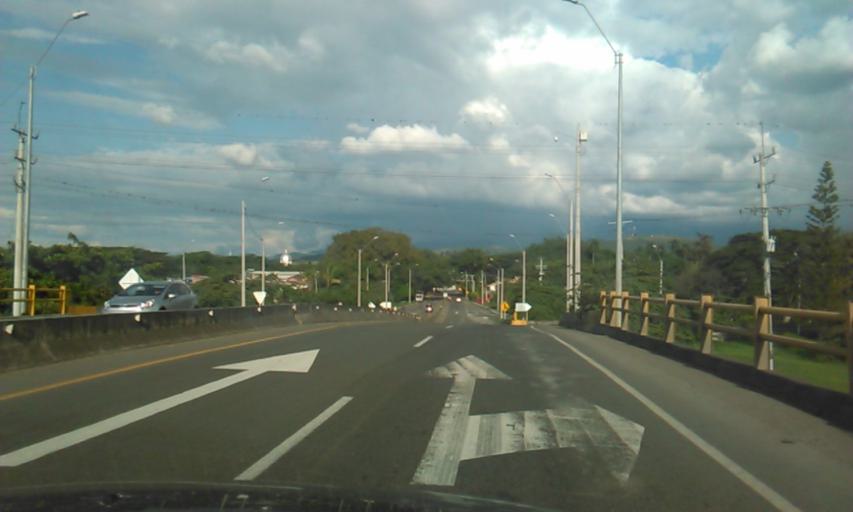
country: CO
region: Valle del Cauca
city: Buga
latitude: 3.8933
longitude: -76.3122
